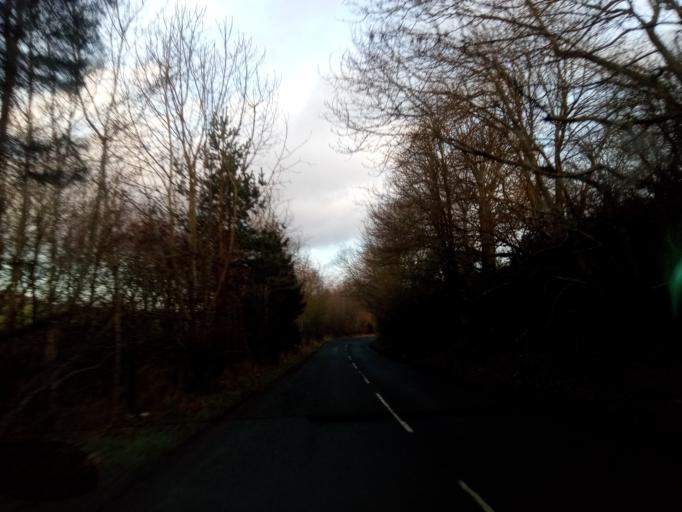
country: GB
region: Scotland
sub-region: The Scottish Borders
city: Melrose
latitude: 55.5551
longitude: -2.7349
